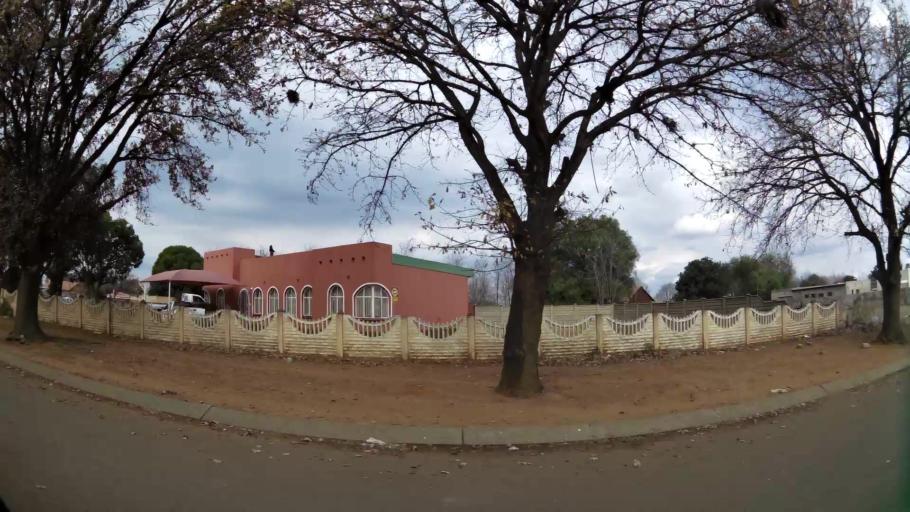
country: ZA
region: Gauteng
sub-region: Sedibeng District Municipality
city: Vanderbijlpark
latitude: -26.7029
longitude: 27.8045
